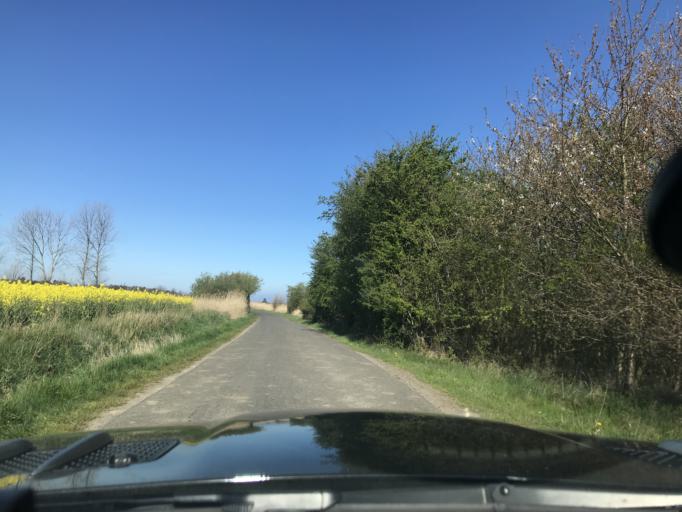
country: DE
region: Schleswig-Holstein
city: Grossenbrode
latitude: 54.4640
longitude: 11.0214
